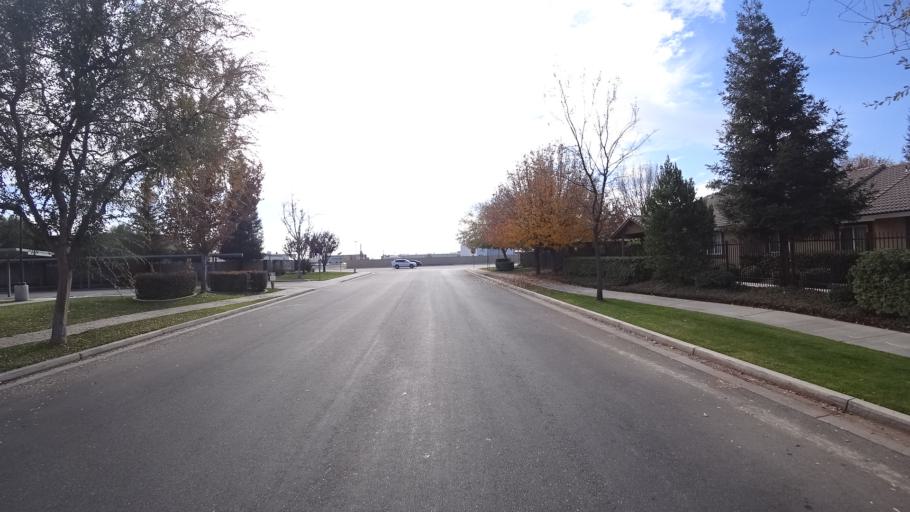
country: US
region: California
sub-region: Kern County
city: Greenacres
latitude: 35.3949
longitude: -119.0896
